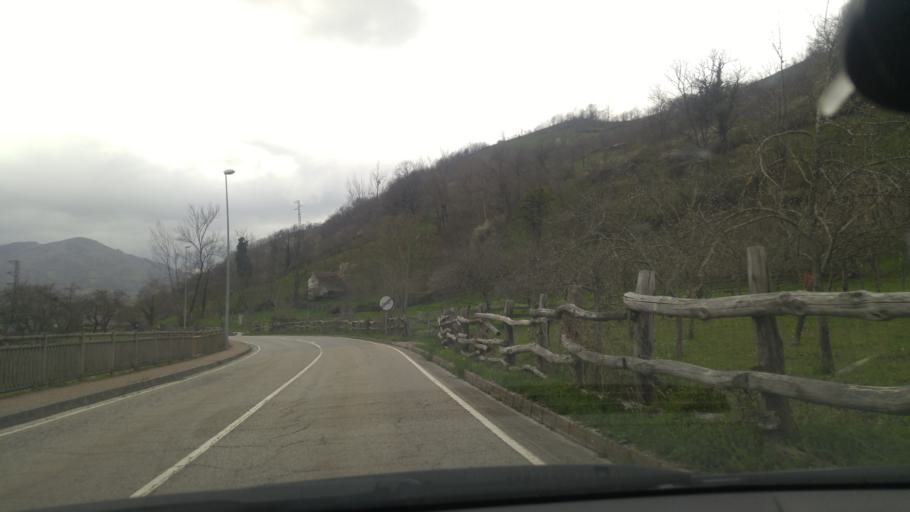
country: ES
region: Asturias
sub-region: Province of Asturias
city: Rio Aller
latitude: 43.1166
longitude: -5.5340
